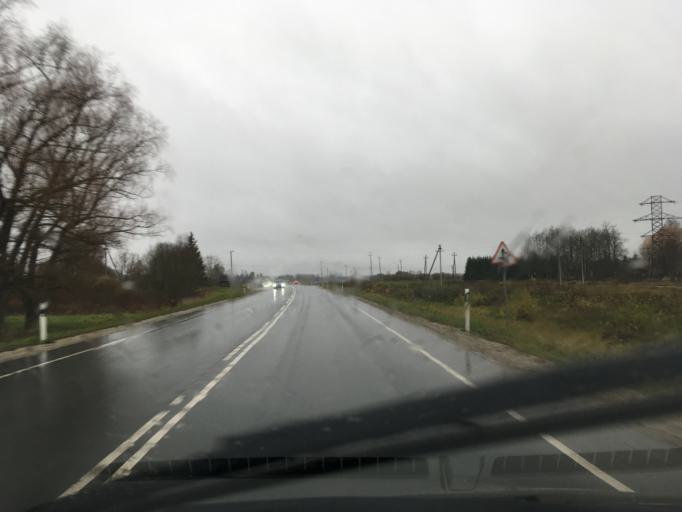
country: EE
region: Harju
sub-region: Nissi vald
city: Turba
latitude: 58.8853
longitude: 24.0899
